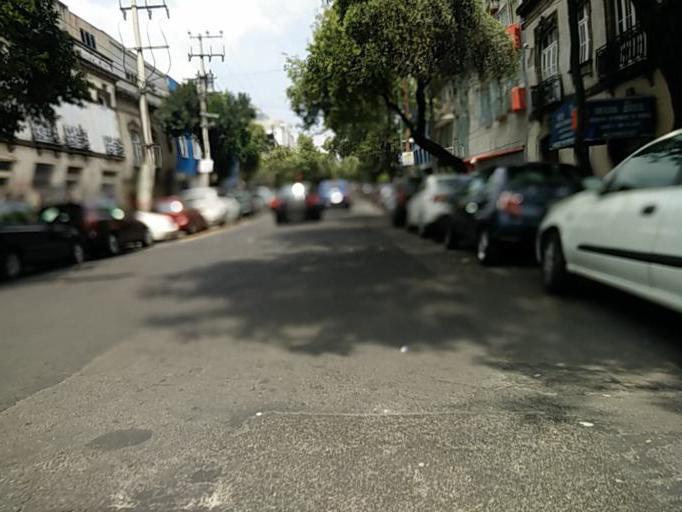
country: MX
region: Mexico City
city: Benito Juarez
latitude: 19.4149
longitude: -99.1603
